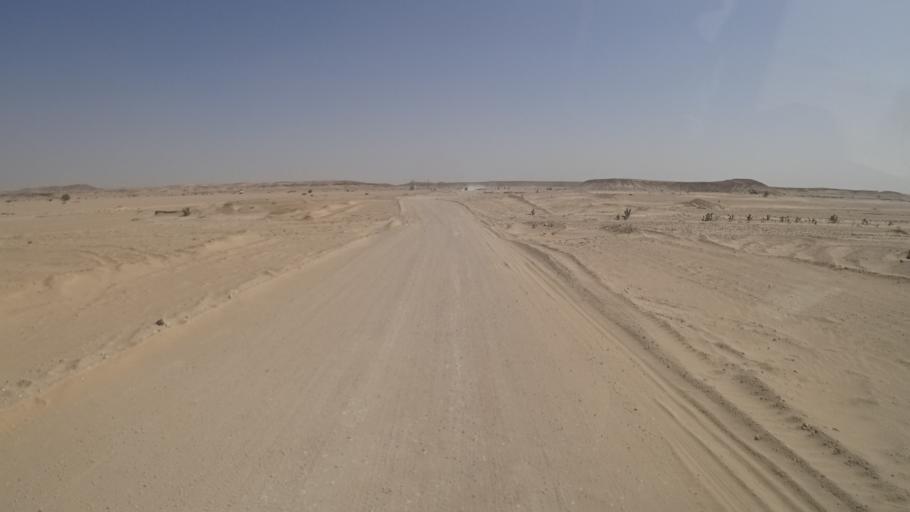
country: YE
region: Al Mahrah
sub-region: Shahan
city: Shihan as Sufla
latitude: 17.8754
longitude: 52.6064
